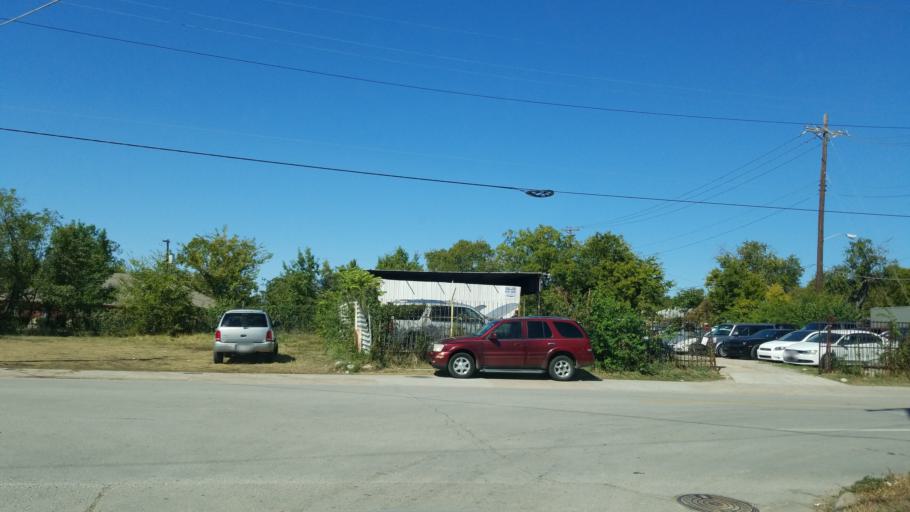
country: US
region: Texas
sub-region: Dallas County
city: Dallas
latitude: 32.7846
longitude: -96.7572
